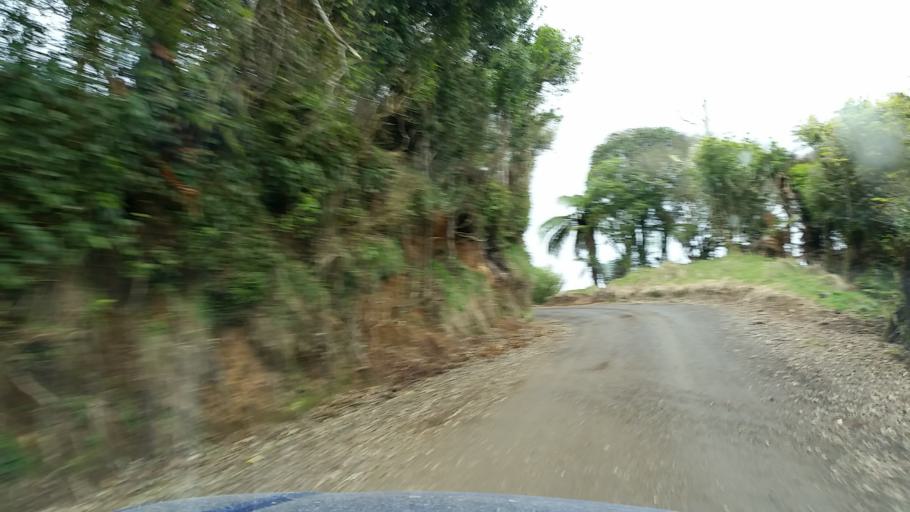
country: NZ
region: Taranaki
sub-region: South Taranaki District
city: Eltham
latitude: -39.1677
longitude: 174.6283
